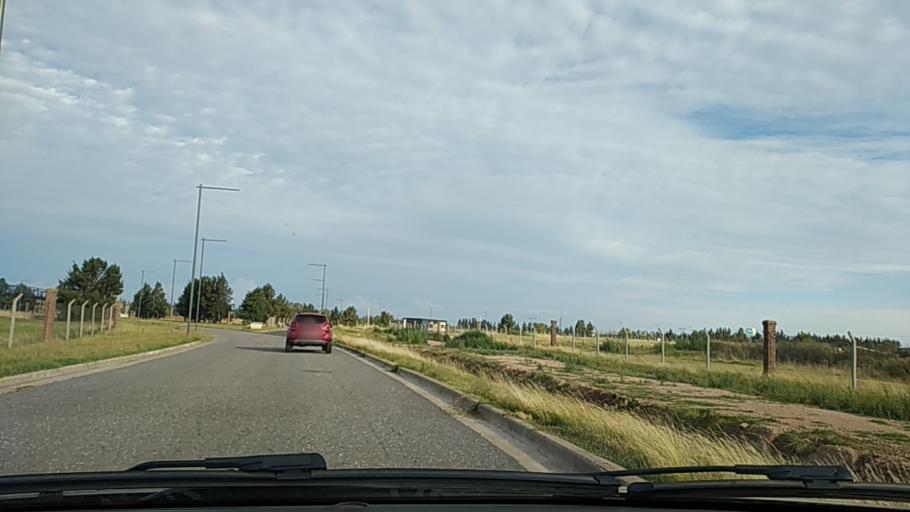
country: AR
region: Santa Fe
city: Funes
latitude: -32.9419
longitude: -60.7716
